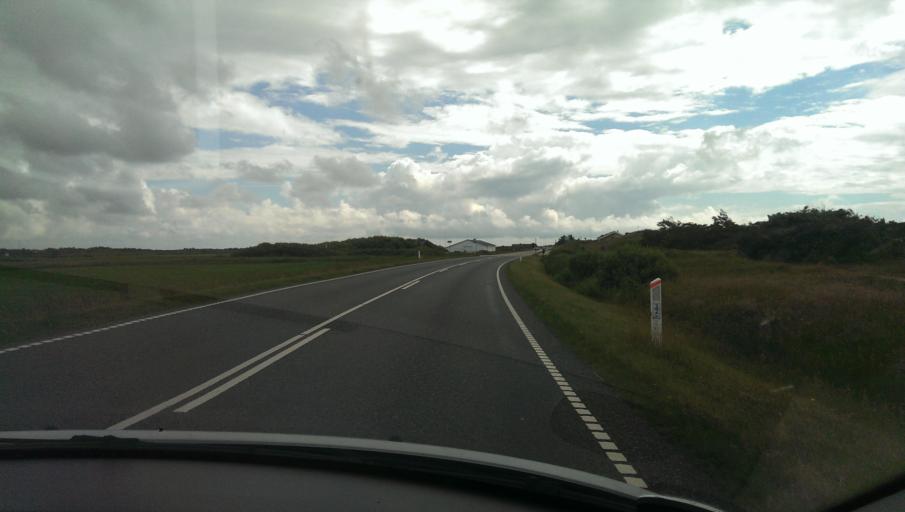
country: DK
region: Central Jutland
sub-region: Ringkobing-Skjern Kommune
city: Ringkobing
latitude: 56.1474
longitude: 8.1260
